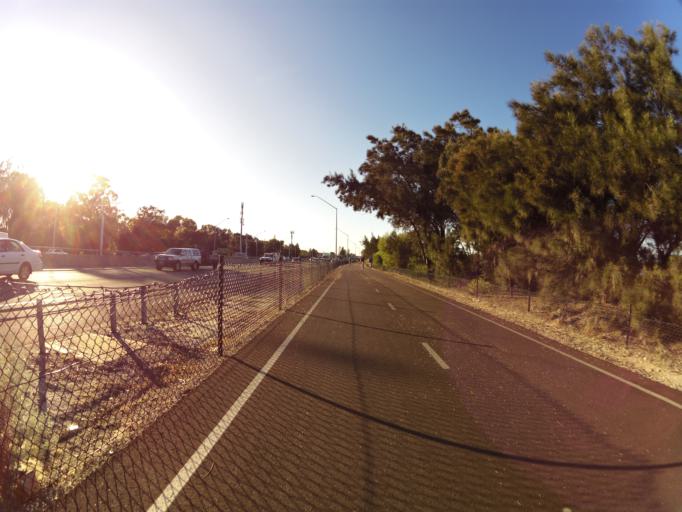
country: AU
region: Western Australia
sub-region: South Perth
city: Como
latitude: -31.9846
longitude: 115.8514
